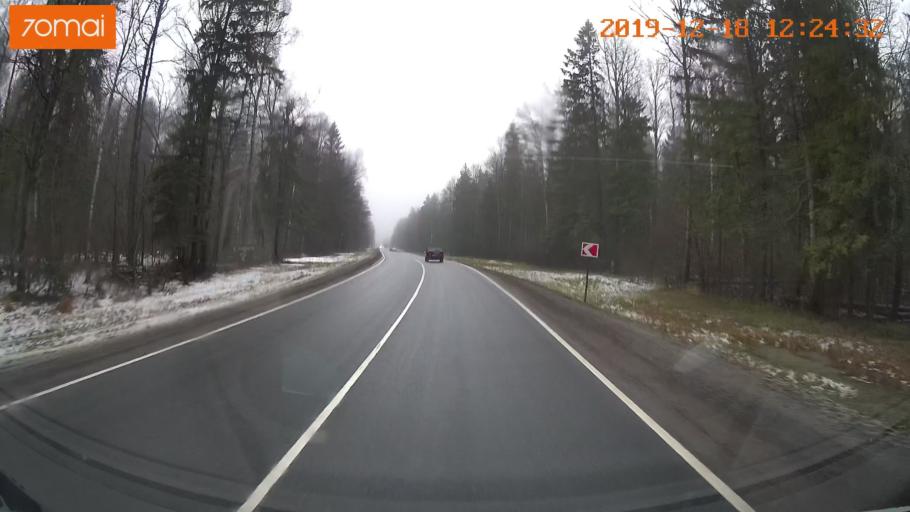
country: RU
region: Moskovskaya
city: Novopetrovskoye
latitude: 56.0259
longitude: 36.5008
